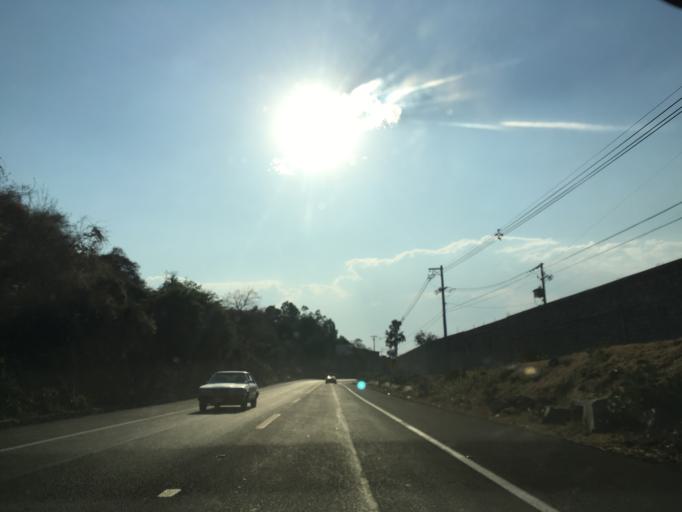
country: MX
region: Michoacan
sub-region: Indaparapeo
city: Colonia de Guadalupe
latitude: 19.8068
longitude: -100.8785
